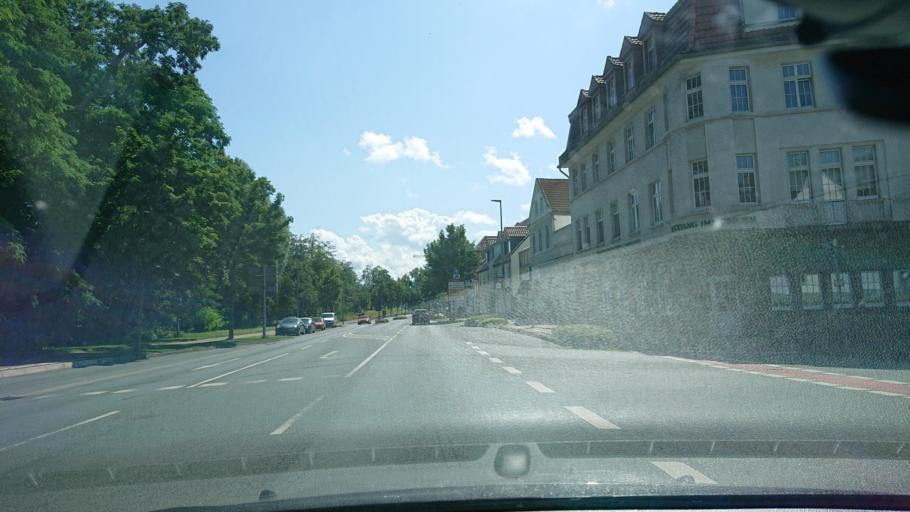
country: DE
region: North Rhine-Westphalia
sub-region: Regierungsbezirk Arnsberg
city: Soest
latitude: 51.5770
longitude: 8.1086
